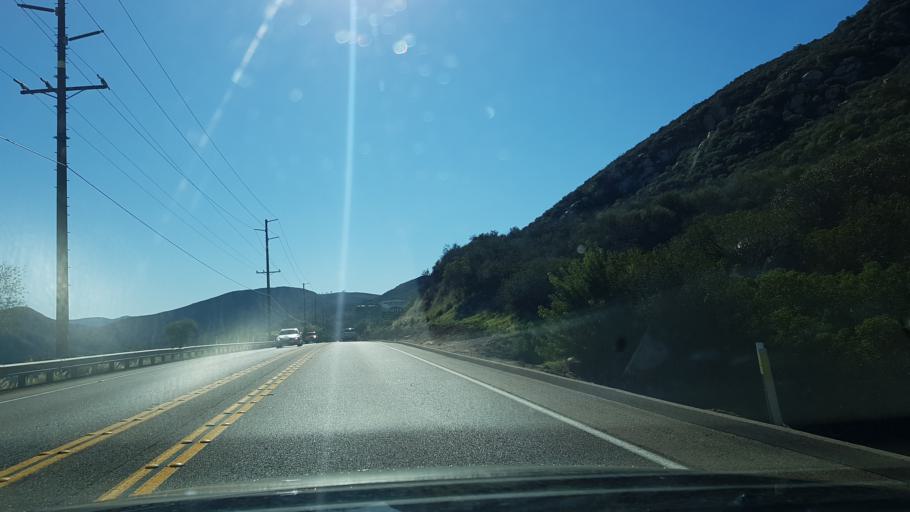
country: US
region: California
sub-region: San Diego County
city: Escondido
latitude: 33.0720
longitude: -117.1216
